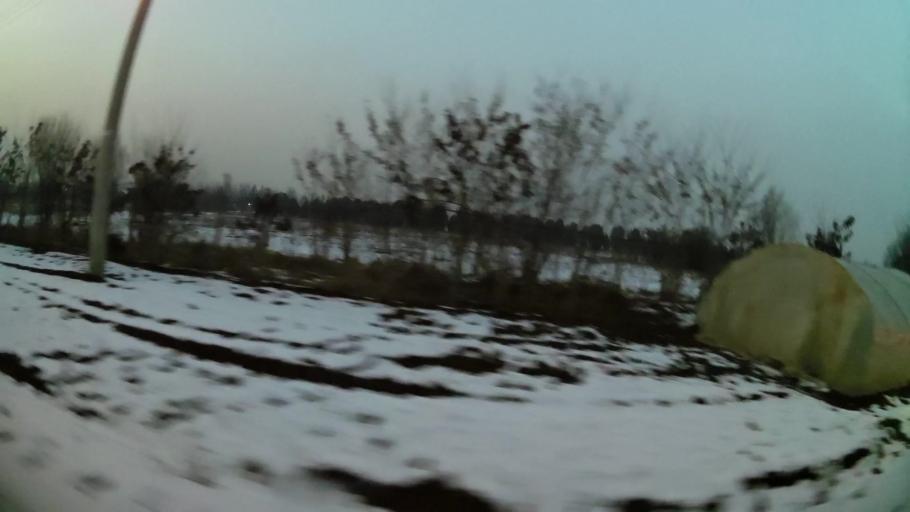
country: MK
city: Creshevo
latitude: 42.0059
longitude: 21.5160
